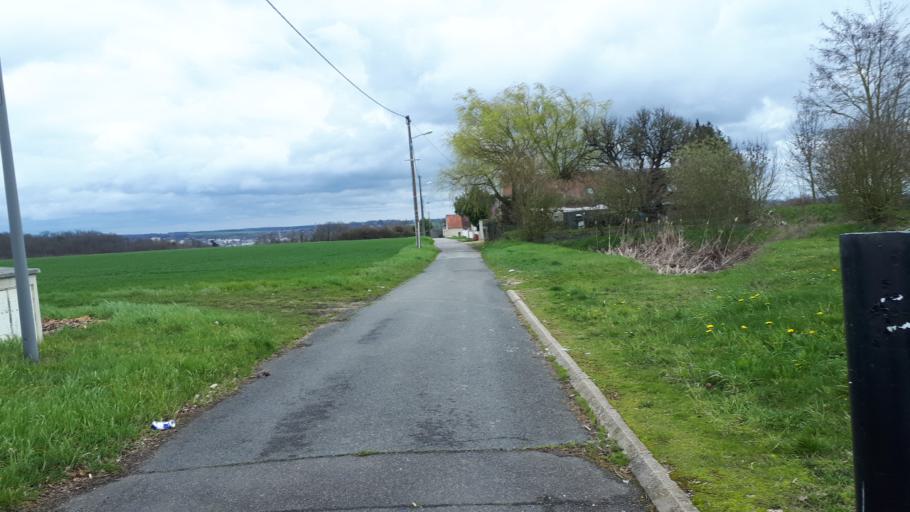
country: FR
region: Centre
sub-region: Departement du Loir-et-Cher
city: Naveil
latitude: 47.8088
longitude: 1.0286
